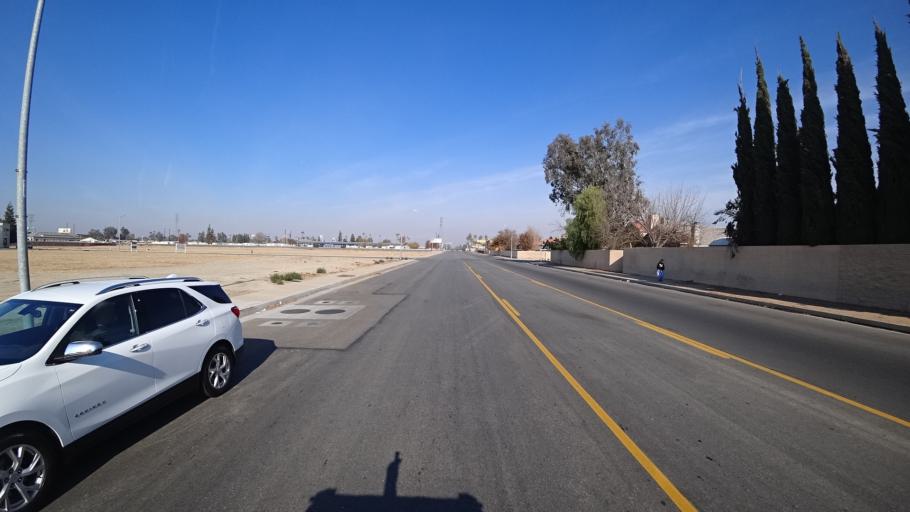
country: US
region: California
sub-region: Kern County
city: Greenfield
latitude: 35.3114
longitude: -119.0302
